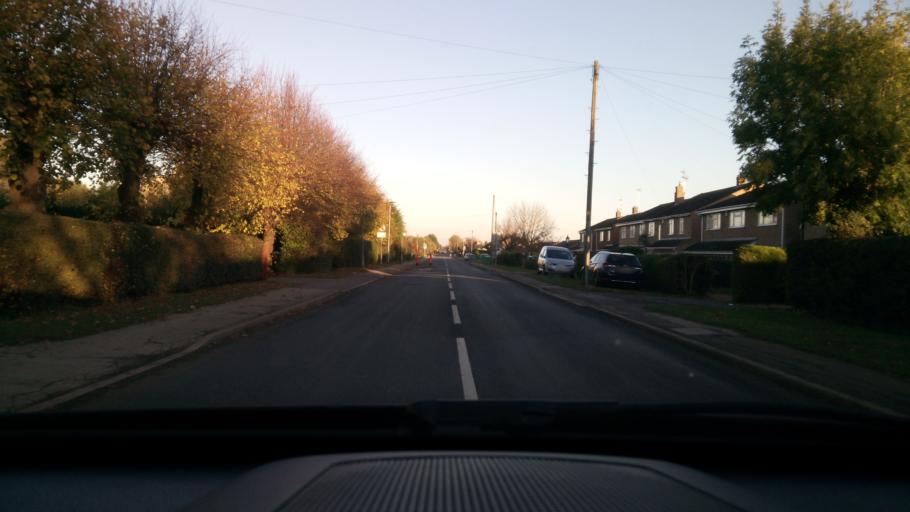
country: GB
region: England
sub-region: Peterborough
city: Helpston
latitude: 52.6356
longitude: -0.3398
